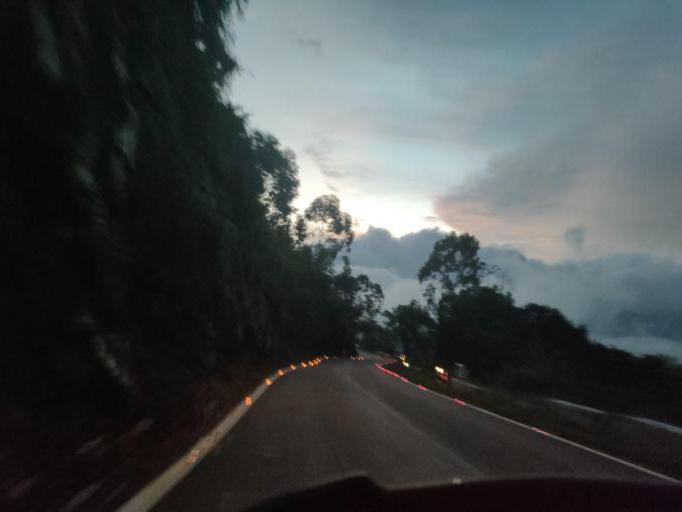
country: IN
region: Tamil Nadu
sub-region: Dindigul
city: Kodaikanal
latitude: 10.2816
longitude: 77.5345
